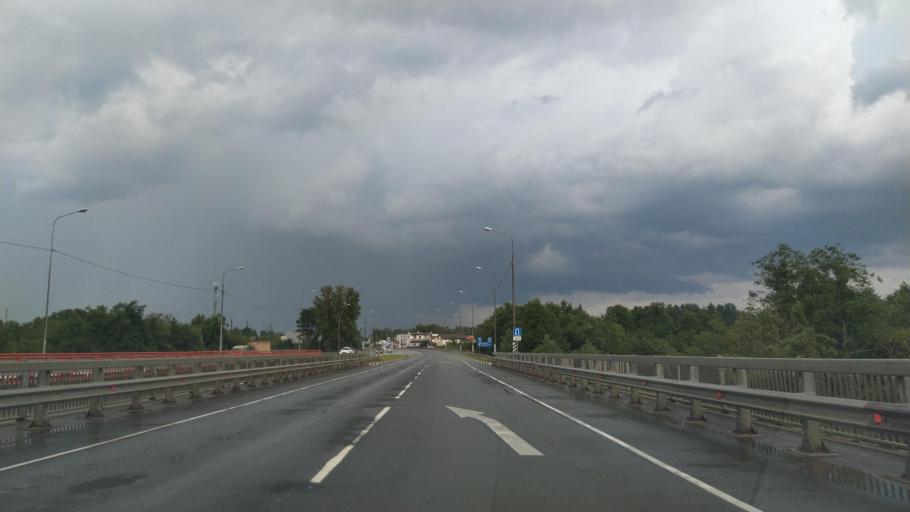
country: RU
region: Pskov
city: Pskov
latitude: 57.7415
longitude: 28.3676
